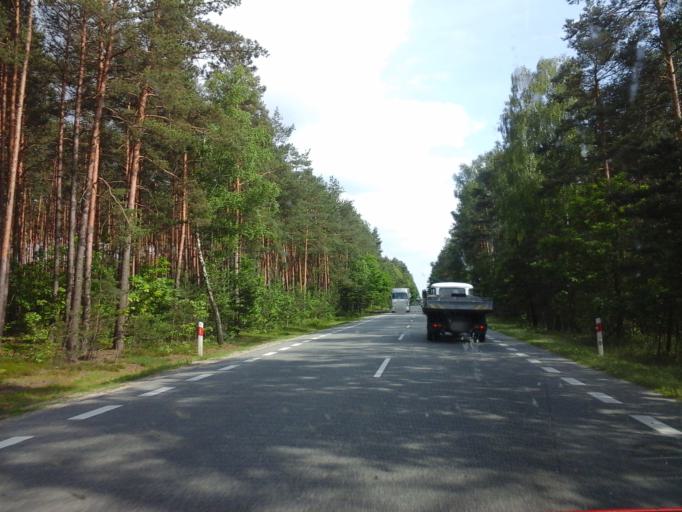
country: PL
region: Swietokrzyskie
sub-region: Powiat konecki
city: Ruda Maleniecka
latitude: 51.1545
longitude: 20.2347
